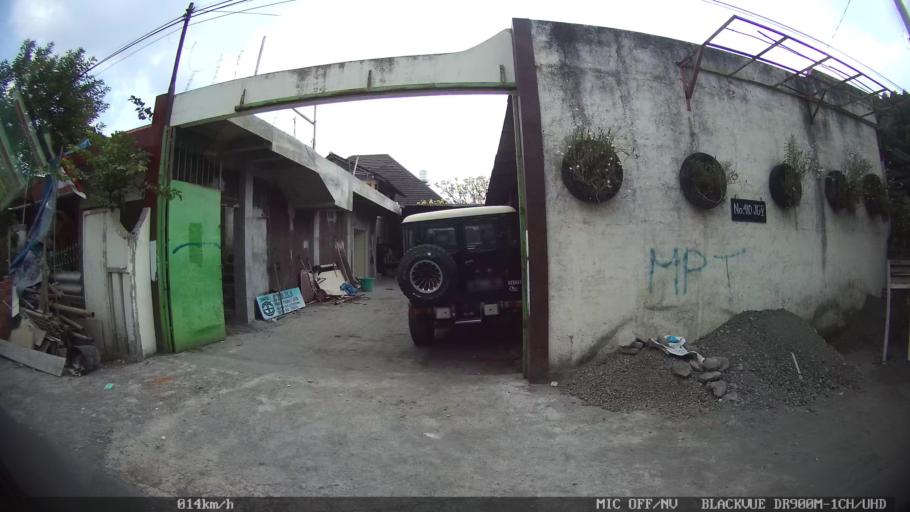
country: ID
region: Daerah Istimewa Yogyakarta
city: Yogyakarta
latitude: -7.8052
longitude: 110.4053
